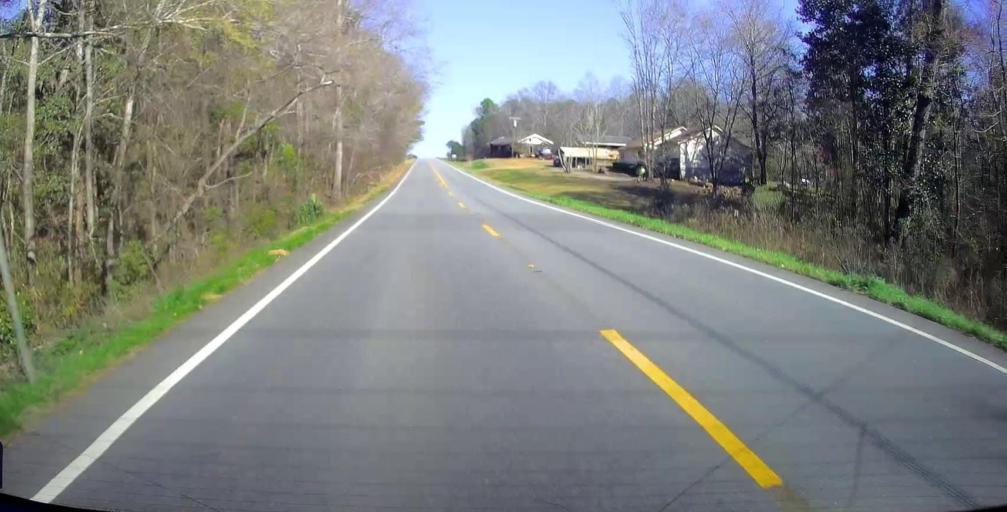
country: US
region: Georgia
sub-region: Dooly County
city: Unadilla
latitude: 32.3391
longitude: -83.8079
